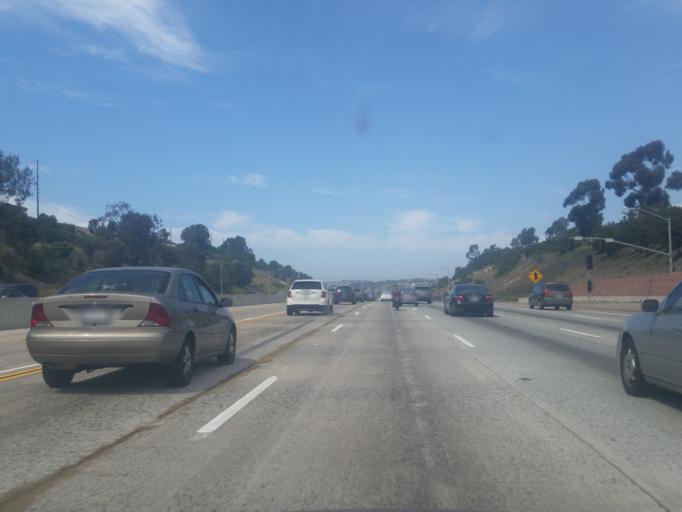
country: US
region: California
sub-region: San Diego County
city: Del Mar
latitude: 32.9513
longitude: -117.2439
